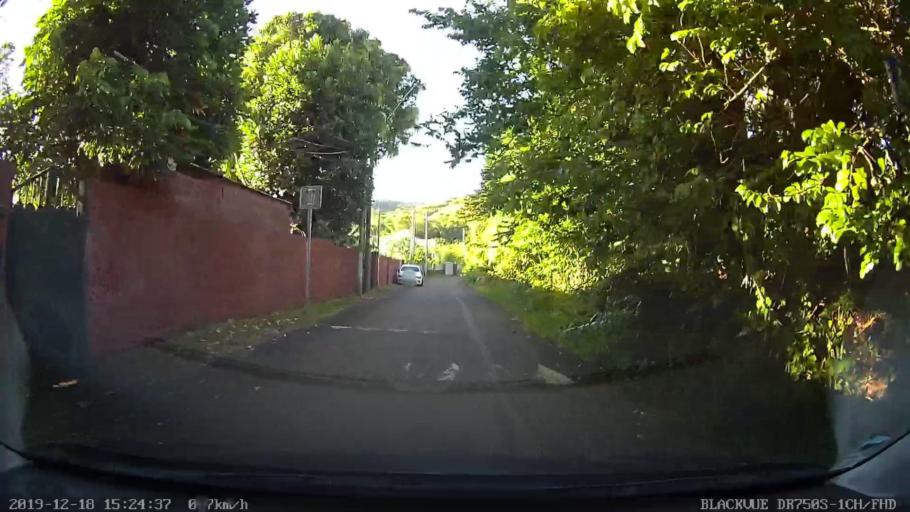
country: RE
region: Reunion
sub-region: Reunion
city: Bras-Panon
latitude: -21.0001
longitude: 55.6537
